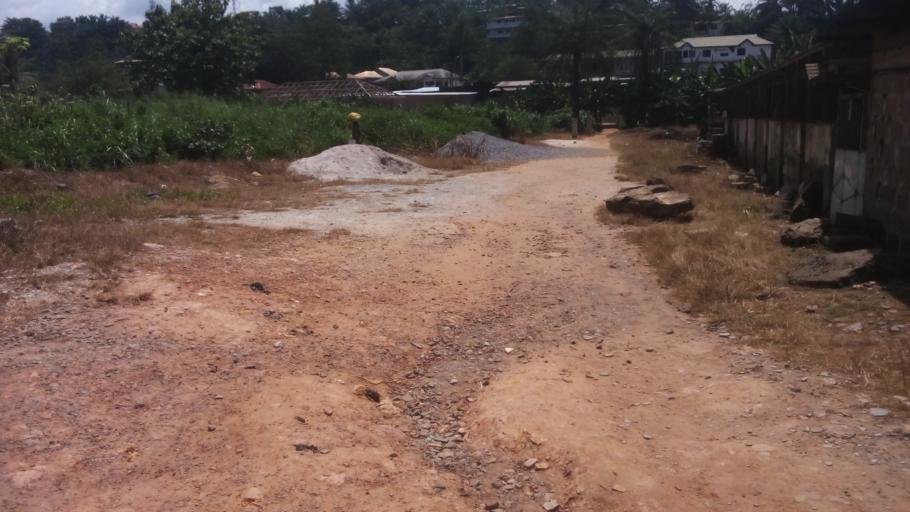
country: GH
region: Western
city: Tarkwa
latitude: 5.3019
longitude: -1.9982
